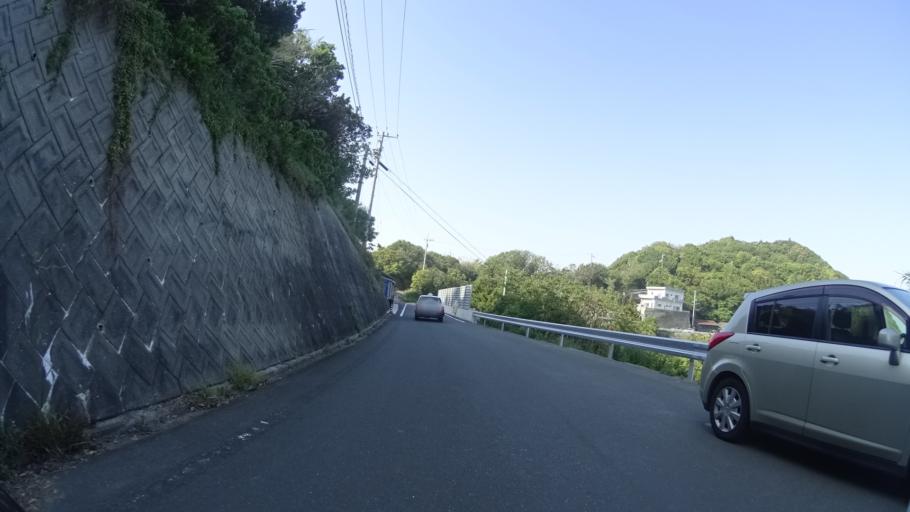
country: JP
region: Oita
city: Tsukumiura
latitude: 33.3482
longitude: 132.0269
